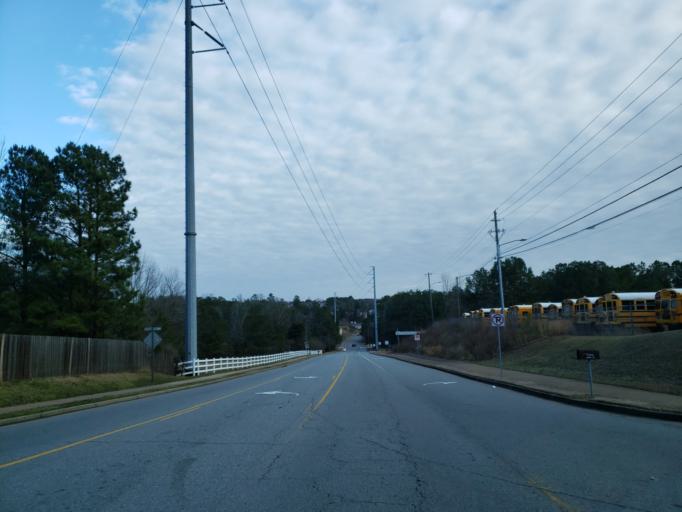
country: US
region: Georgia
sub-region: Cobb County
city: Kennesaw
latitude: 34.0578
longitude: -84.6219
